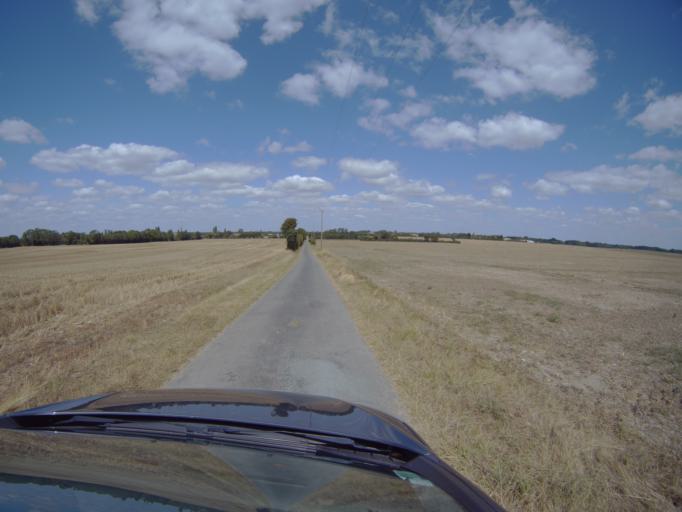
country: FR
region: Poitou-Charentes
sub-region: Departement des Deux-Sevres
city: Saint-Hilaire-la-Palud
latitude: 46.2698
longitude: -0.6542
